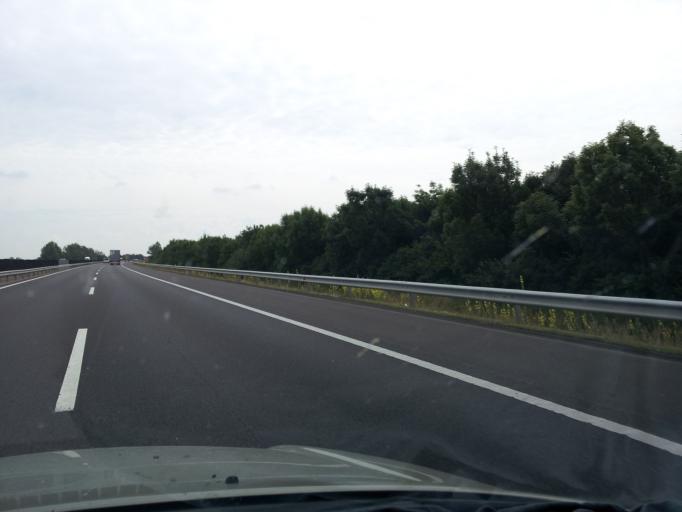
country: HU
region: Heves
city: Kompolt
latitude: 47.7124
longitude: 20.2064
